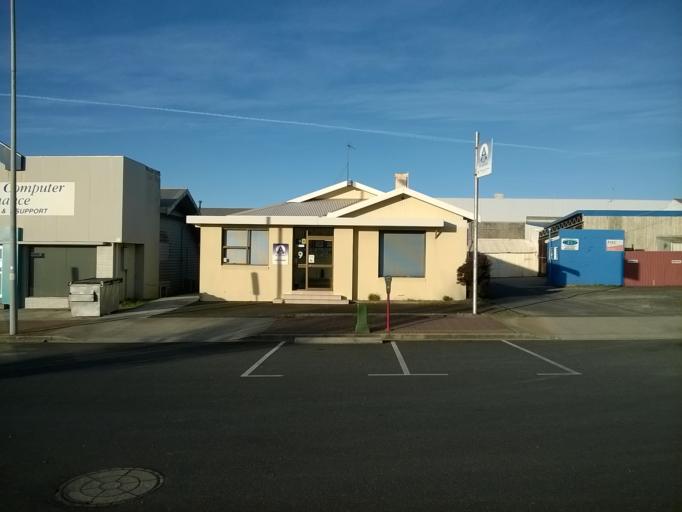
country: AU
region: Tasmania
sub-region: Burnie
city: Burnie
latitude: -41.0501
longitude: 145.9024
